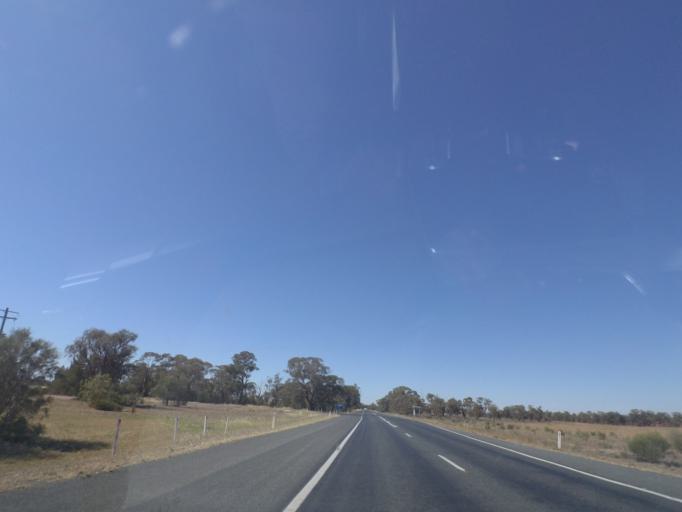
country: AU
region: New South Wales
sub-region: Bland
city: West Wyalong
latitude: -34.1928
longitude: 147.1114
